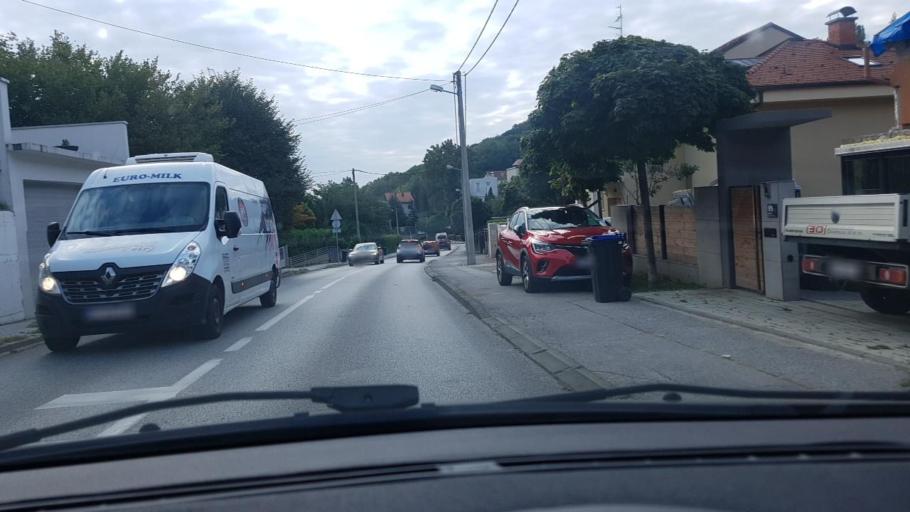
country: HR
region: Grad Zagreb
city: Zagreb
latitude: 45.8478
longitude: 15.9634
